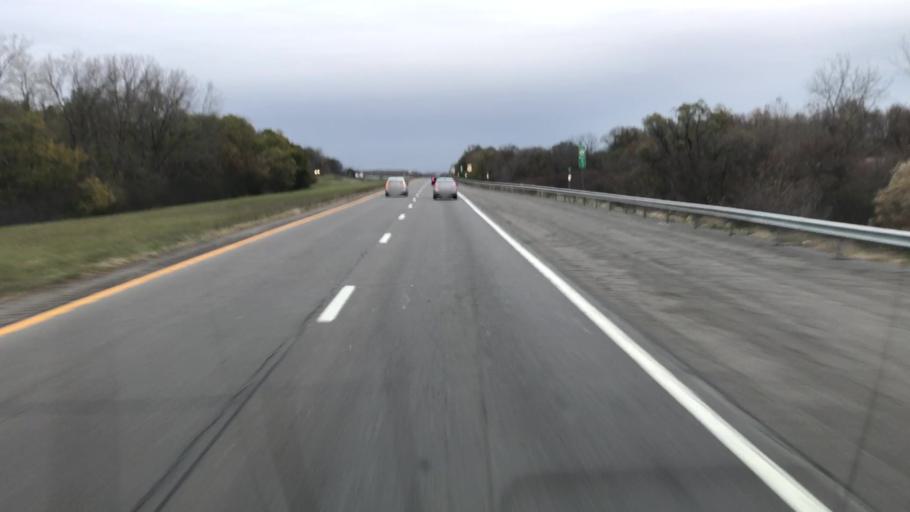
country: US
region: New York
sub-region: Onondaga County
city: Camillus
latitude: 43.0355
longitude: -76.3221
